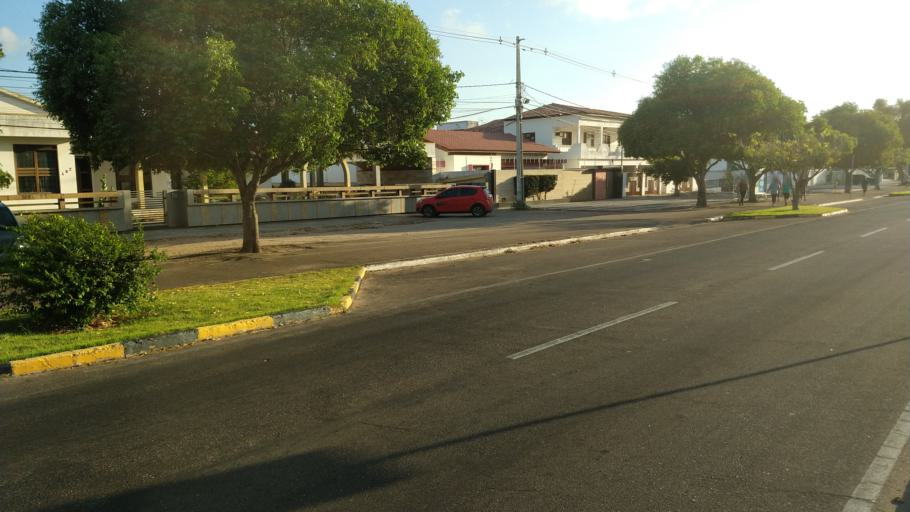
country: BR
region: Bahia
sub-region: Paulo Afonso
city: Paulo Afonso
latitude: -9.3984
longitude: -38.2234
